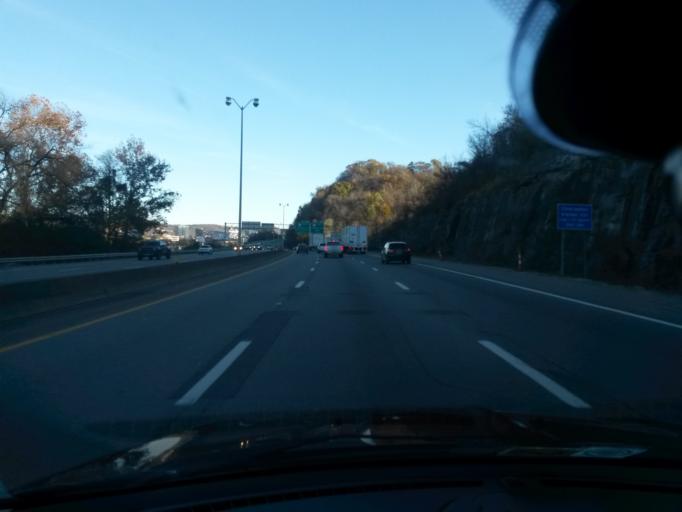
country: US
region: West Virginia
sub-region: Kanawha County
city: Charleston
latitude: 38.3589
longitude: -81.6624
